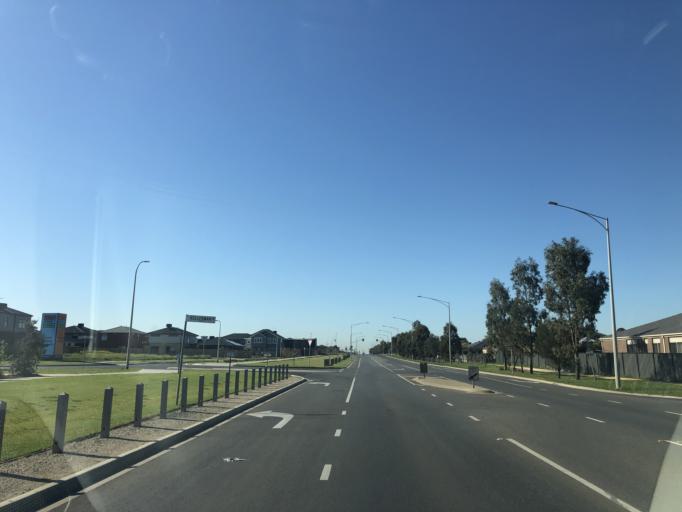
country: AU
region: Victoria
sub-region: Wyndham
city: Hoppers Crossing
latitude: -37.8947
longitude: 144.7171
